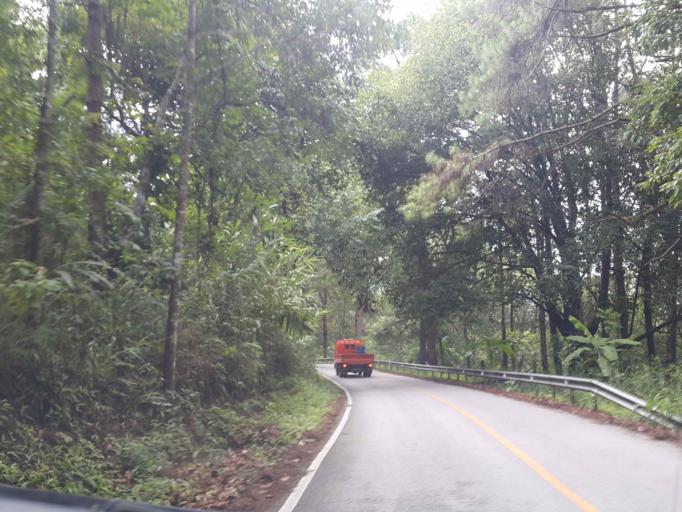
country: TH
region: Chiang Mai
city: Mae Chaem
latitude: 18.5175
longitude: 98.4634
